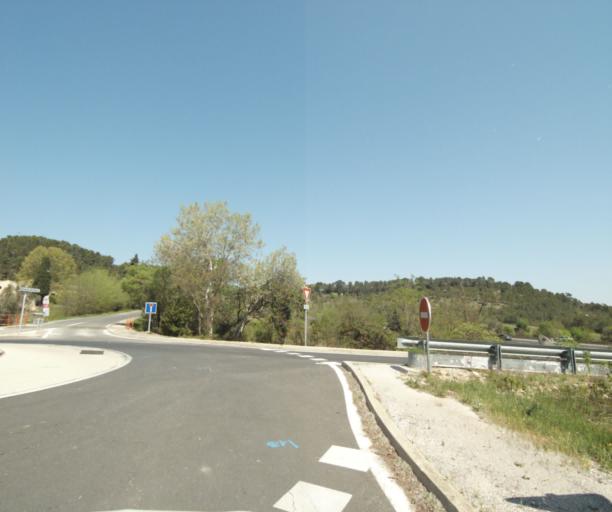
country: FR
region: Languedoc-Roussillon
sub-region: Departement de l'Herault
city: Saint-Clement-de-Riviere
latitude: 43.6582
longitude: 3.8303
